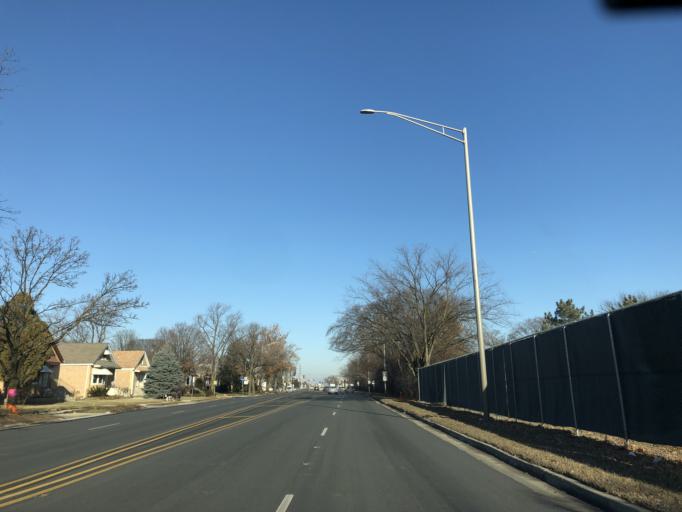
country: US
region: Illinois
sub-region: Cook County
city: North Riverside
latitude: 41.8471
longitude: -87.8327
